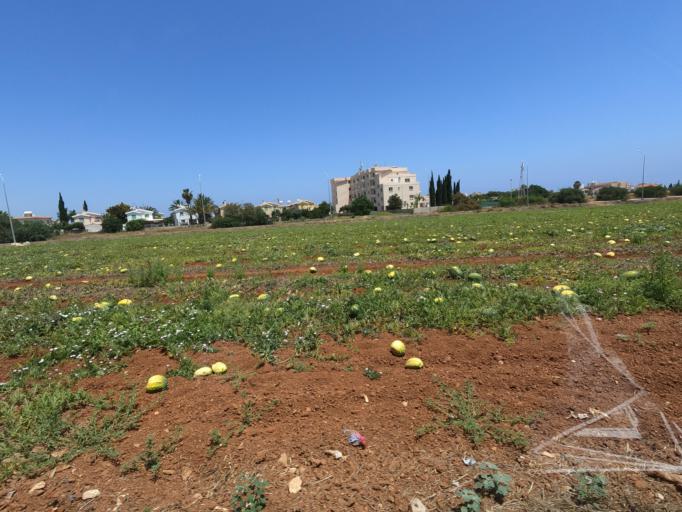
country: CY
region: Ammochostos
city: Protaras
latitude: 35.0303
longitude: 34.0312
